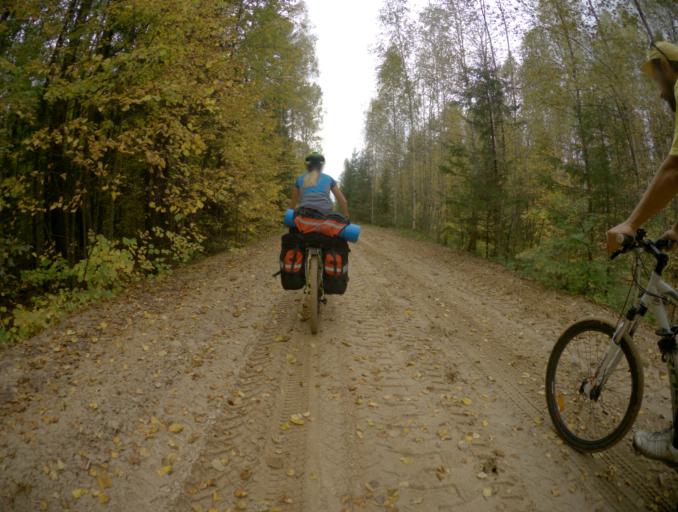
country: RU
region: Vladimir
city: Kideksha
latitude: 56.5002
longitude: 40.7654
